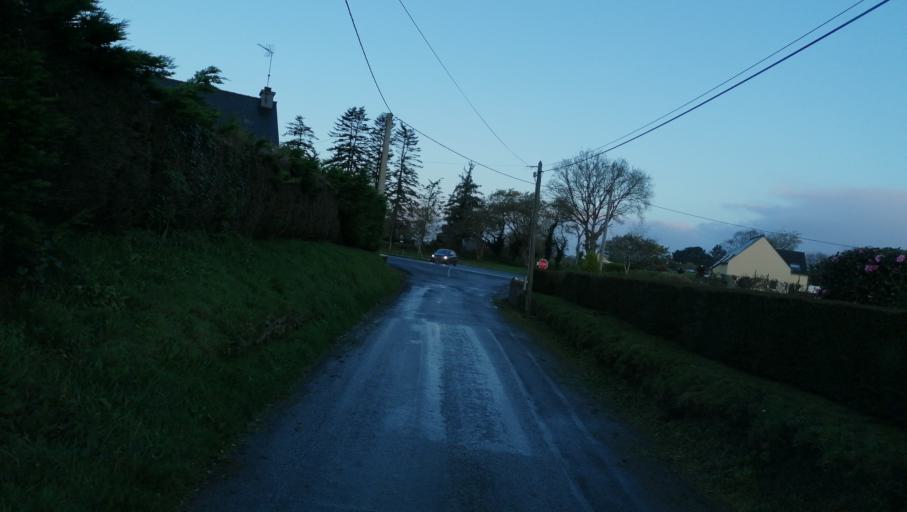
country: FR
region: Brittany
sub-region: Departement des Cotes-d'Armor
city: Plouha
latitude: 48.6670
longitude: -2.9461
